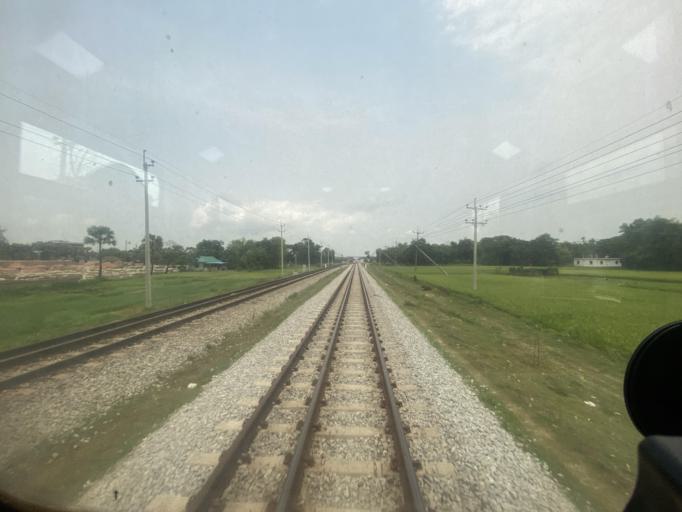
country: BD
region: Chittagong
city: Laksham
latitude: 23.3501
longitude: 91.1501
